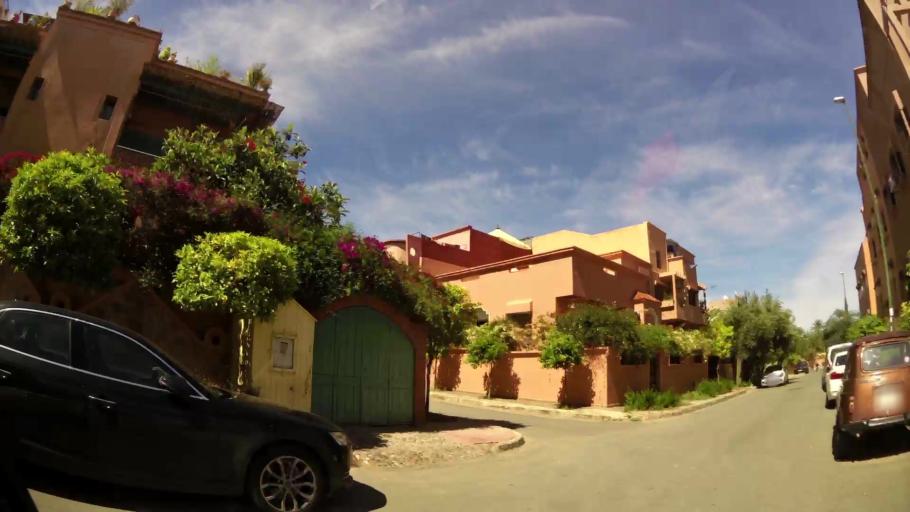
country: MA
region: Marrakech-Tensift-Al Haouz
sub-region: Marrakech
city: Marrakesh
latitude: 31.6649
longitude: -8.0050
